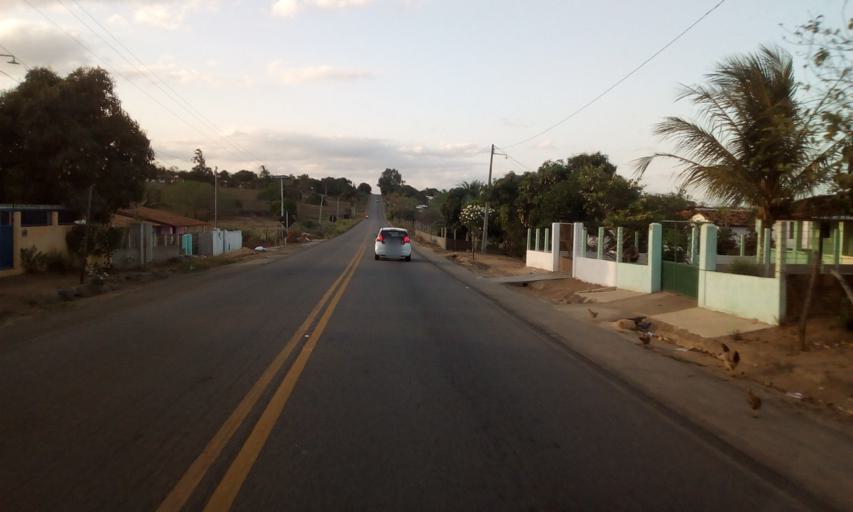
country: BR
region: Paraiba
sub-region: Guarabira
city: Guarabira
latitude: -6.9025
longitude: -35.4585
